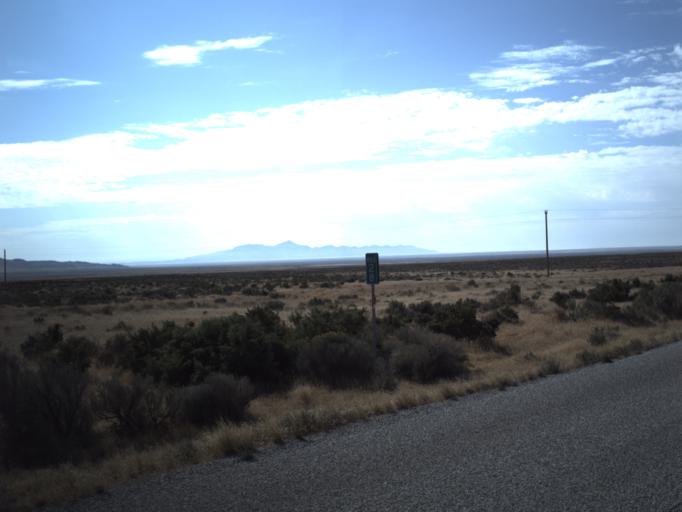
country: US
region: Utah
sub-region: Tooele County
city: Wendover
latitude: 41.5399
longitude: -113.5906
